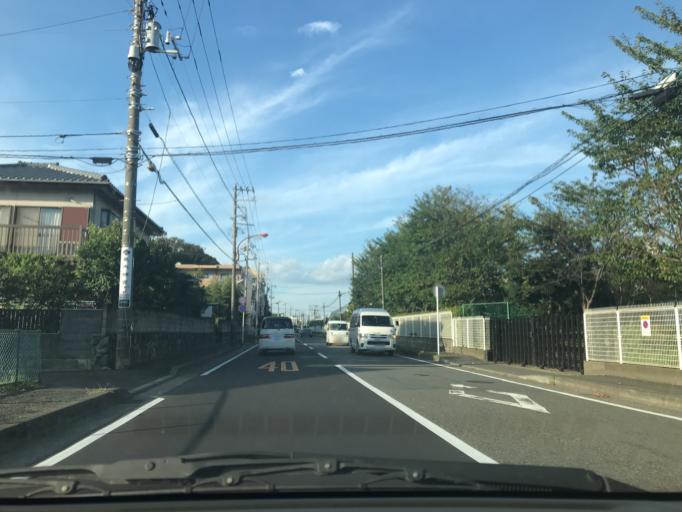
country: JP
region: Kanagawa
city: Fujisawa
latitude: 35.3400
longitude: 139.4728
